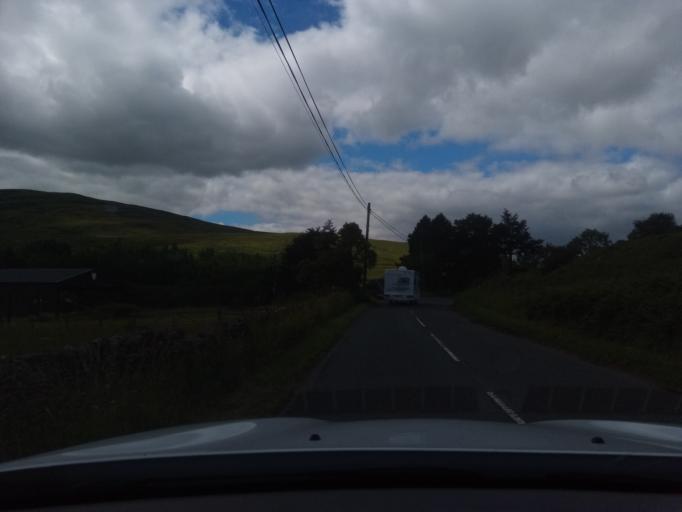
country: GB
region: Scotland
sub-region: The Scottish Borders
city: Innerleithen
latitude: 55.5395
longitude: -3.0050
